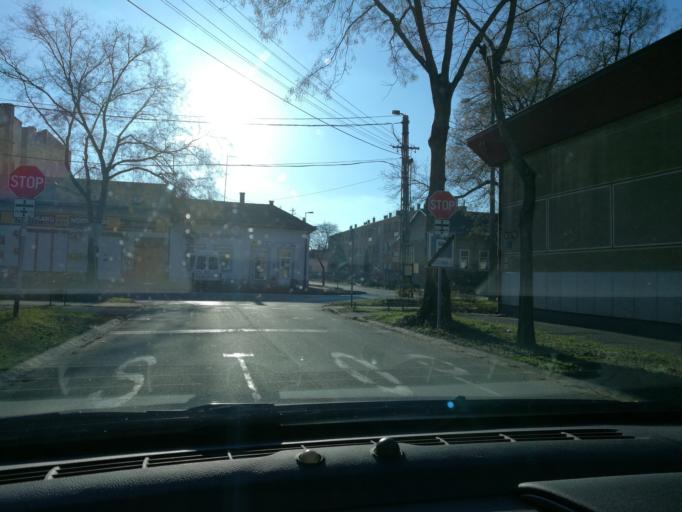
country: HU
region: Szabolcs-Szatmar-Bereg
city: Nyiregyhaza
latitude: 47.9557
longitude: 21.7094
